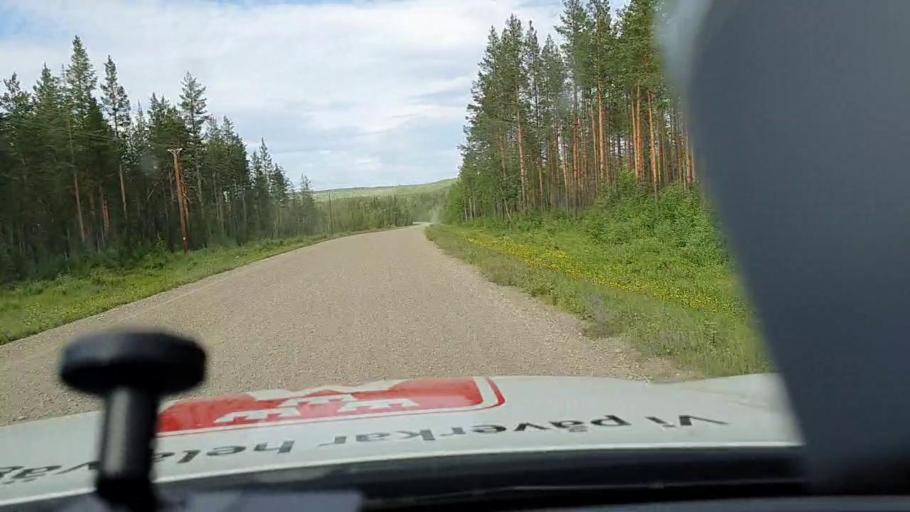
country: SE
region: Norrbotten
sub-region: Alvsbyns Kommun
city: AElvsbyn
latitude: 66.1458
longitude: 21.0219
